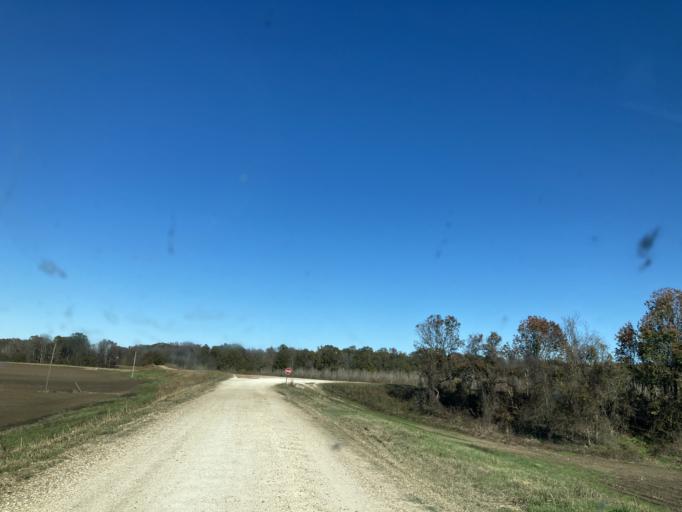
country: US
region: Mississippi
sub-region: Yazoo County
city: Yazoo City
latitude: 32.7765
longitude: -90.6381
